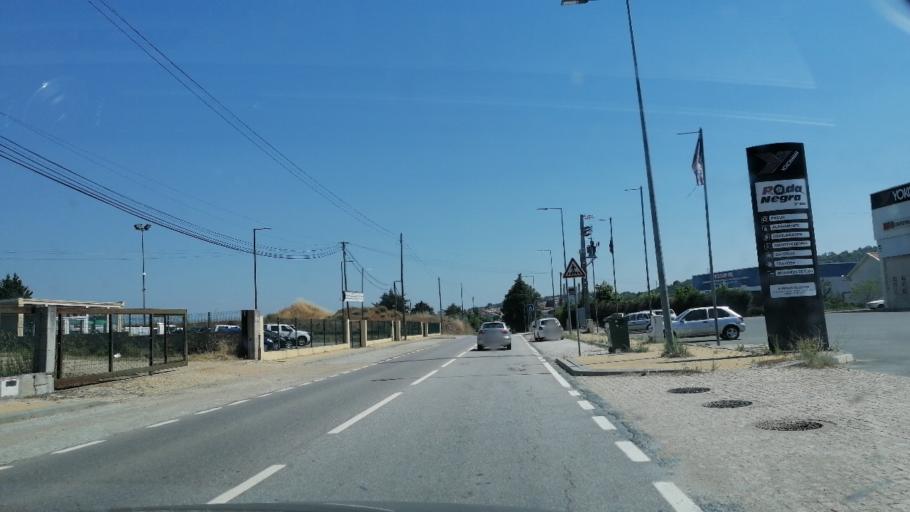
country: PT
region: Braganca
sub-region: Braganca Municipality
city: Braganca
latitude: 41.7736
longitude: -6.7887
